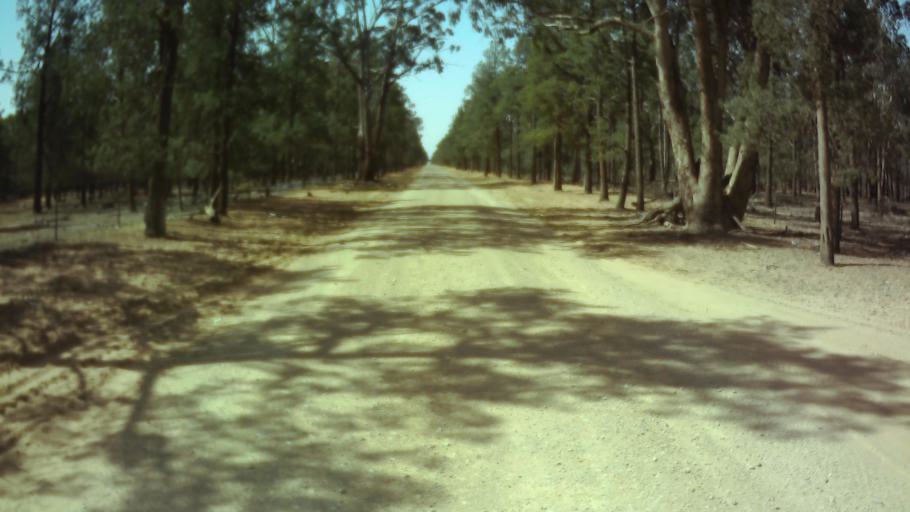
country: AU
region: New South Wales
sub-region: Weddin
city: Grenfell
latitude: -33.9753
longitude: 147.9295
